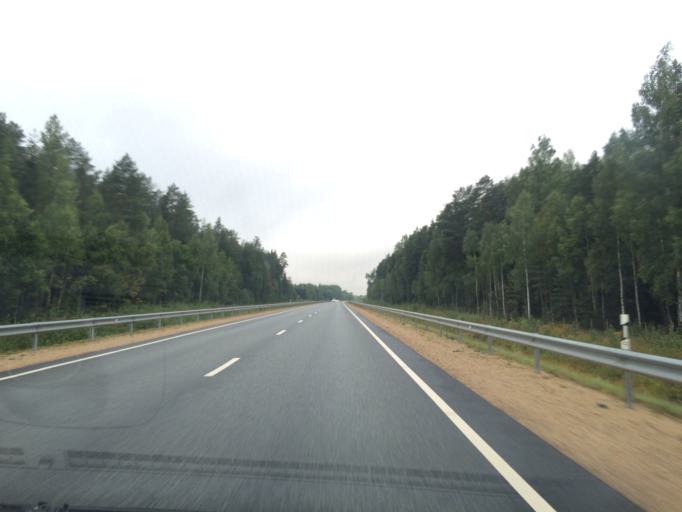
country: LV
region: Lielvarde
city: Lielvarde
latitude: 56.8026
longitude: 24.9138
